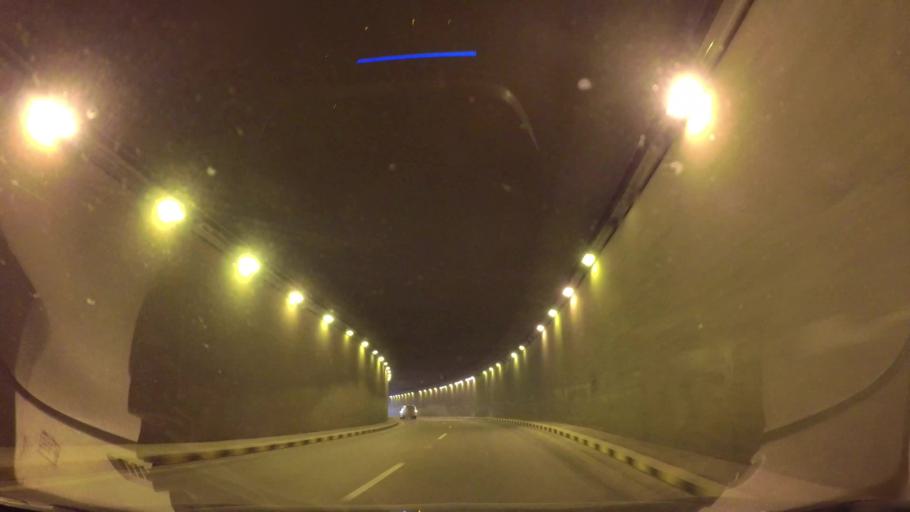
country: JO
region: Amman
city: Amman
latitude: 31.9664
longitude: 35.8995
